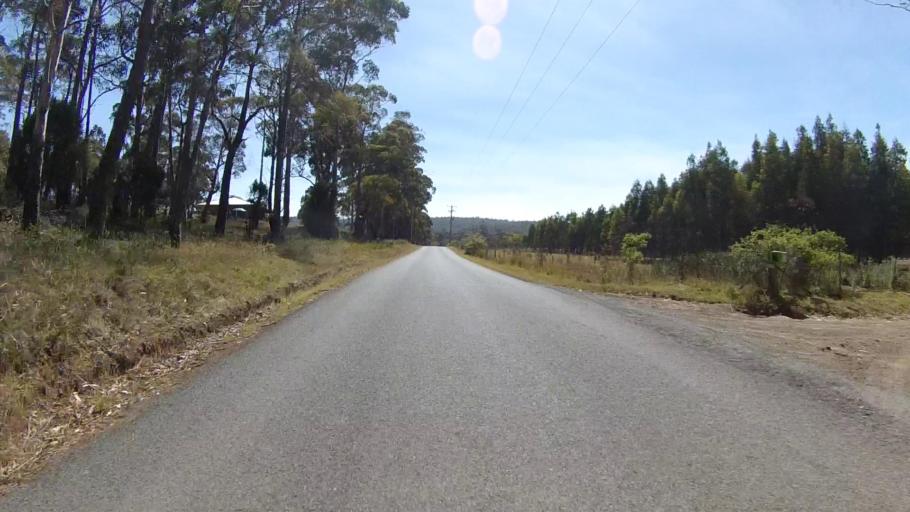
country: AU
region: Tasmania
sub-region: Sorell
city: Sorell
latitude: -42.7503
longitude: 147.7157
